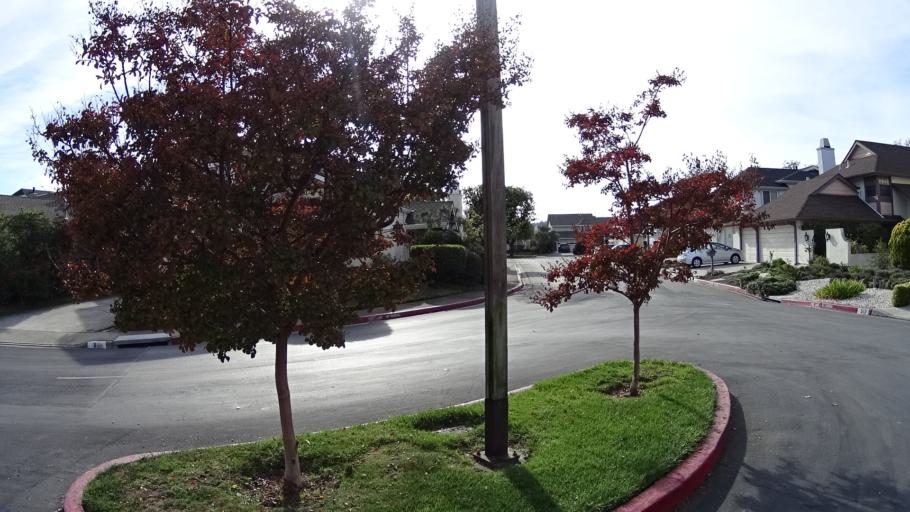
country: US
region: California
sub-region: San Mateo County
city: Redwood Shores
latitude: 37.5399
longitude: -122.2642
